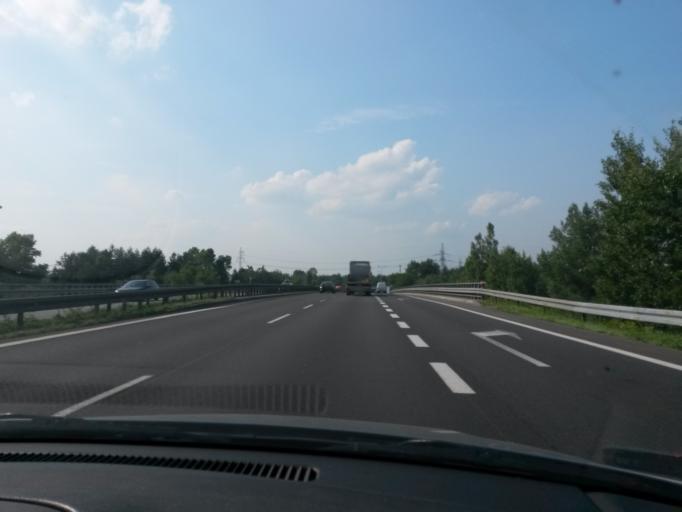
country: PL
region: Silesian Voivodeship
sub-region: Myslowice
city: Myslowice
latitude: 50.2244
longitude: 19.1703
